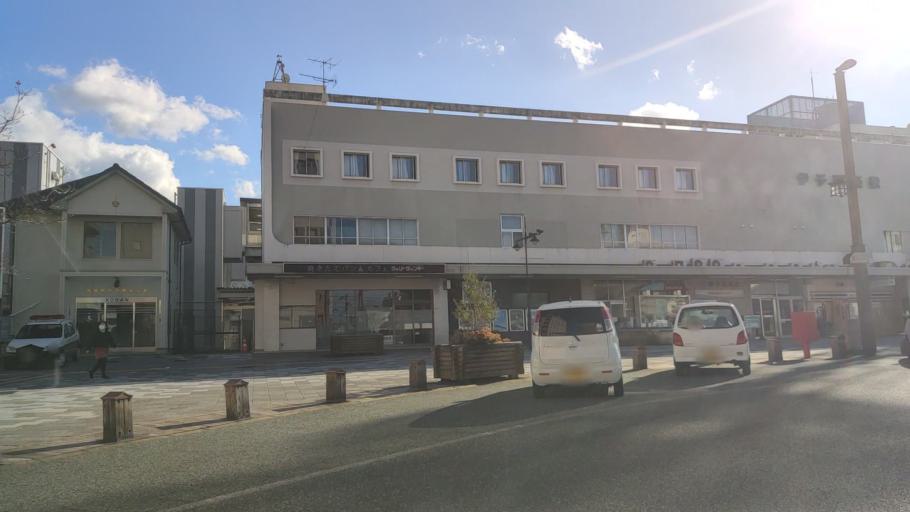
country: JP
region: Ehime
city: Saijo
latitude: 33.9129
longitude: 133.1876
